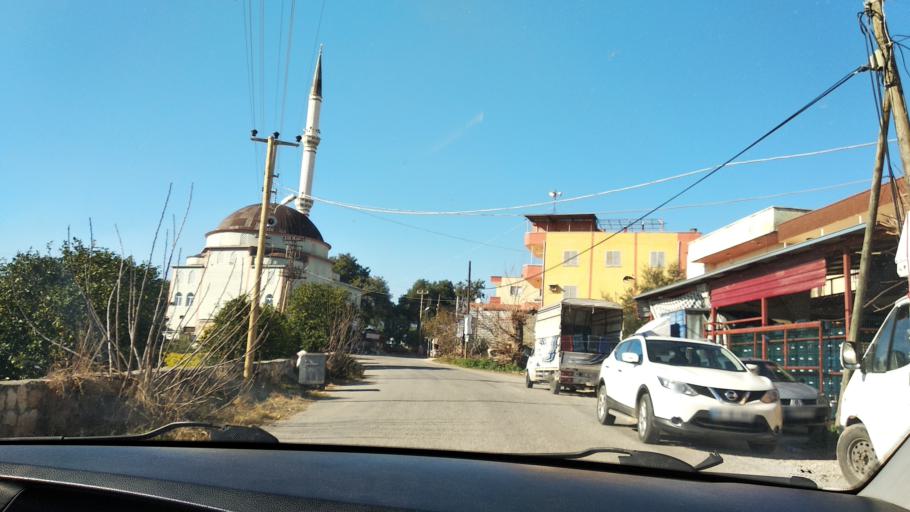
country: TR
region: Mersin
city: Tomuk
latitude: 36.6678
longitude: 34.3578
